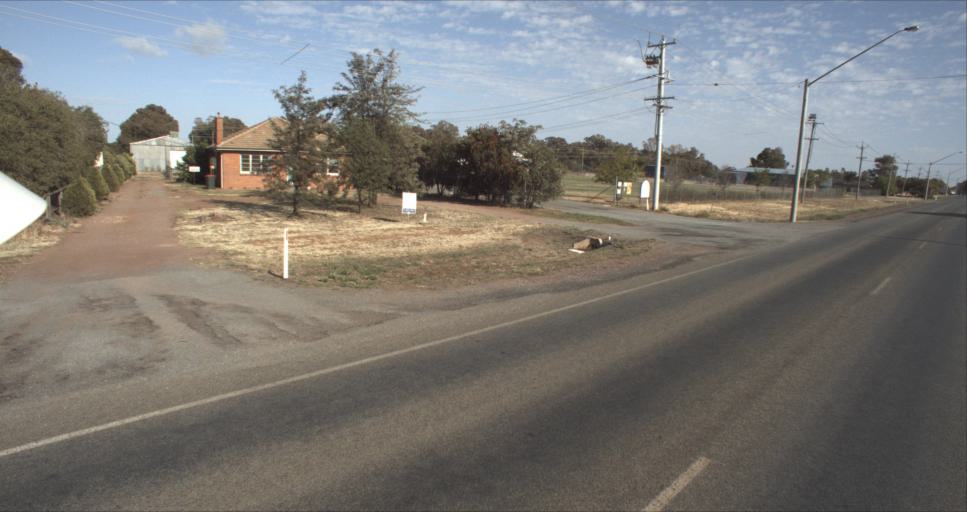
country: AU
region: New South Wales
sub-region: Leeton
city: Leeton
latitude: -34.5652
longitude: 146.3932
